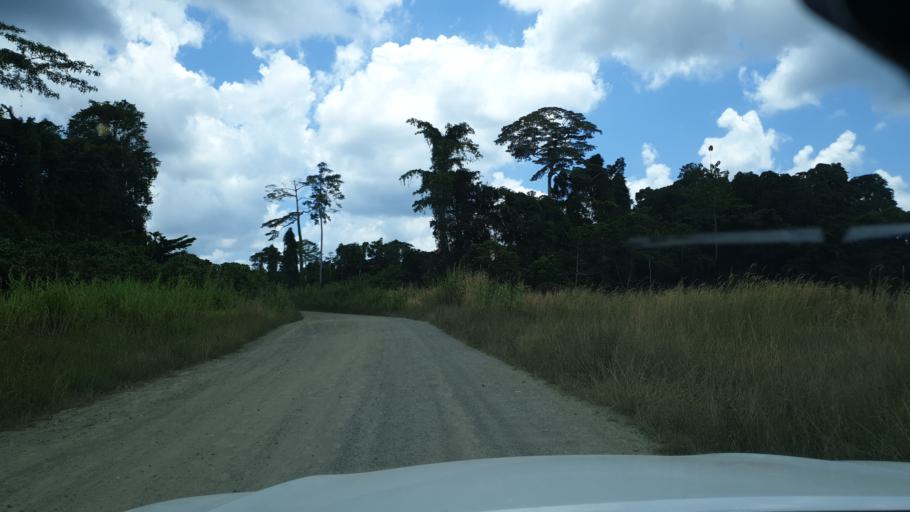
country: PG
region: East Sepik
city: Angoram
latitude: -3.8168
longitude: 143.8517
